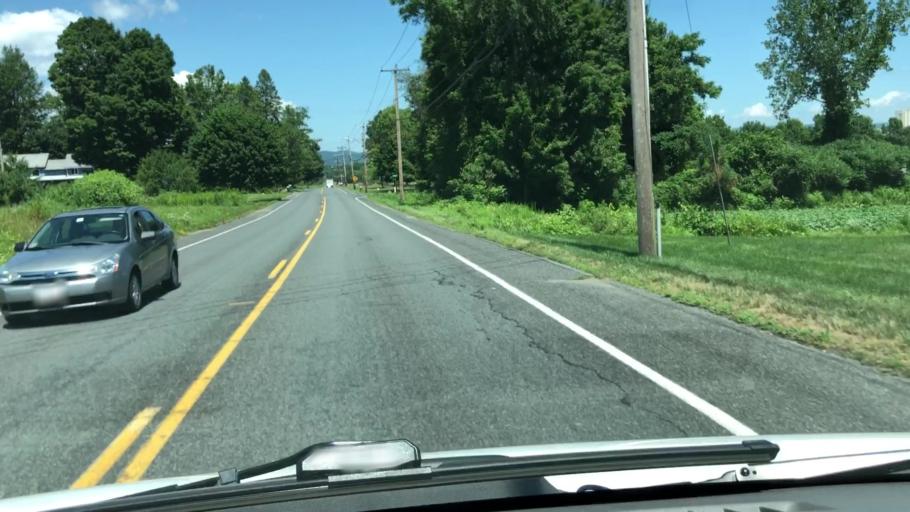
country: US
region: Massachusetts
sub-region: Hampshire County
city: Amherst Center
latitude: 42.3748
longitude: -72.5489
